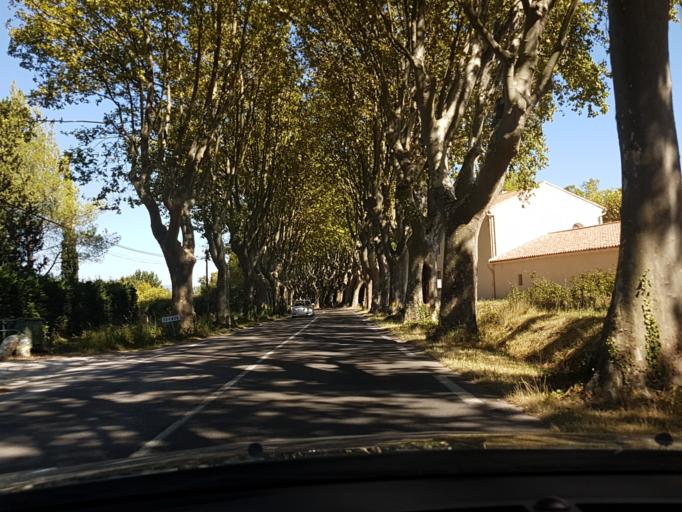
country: FR
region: Provence-Alpes-Cote d'Azur
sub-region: Departement des Bouches-du-Rhone
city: Saint-Remy-de-Provence
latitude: 43.7846
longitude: 4.8738
